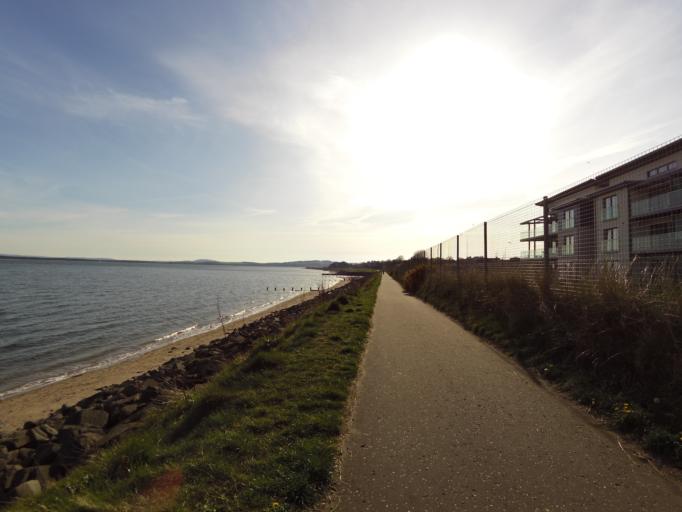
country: GB
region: Scotland
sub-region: Fife
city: Tayport
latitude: 56.4762
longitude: -2.8329
